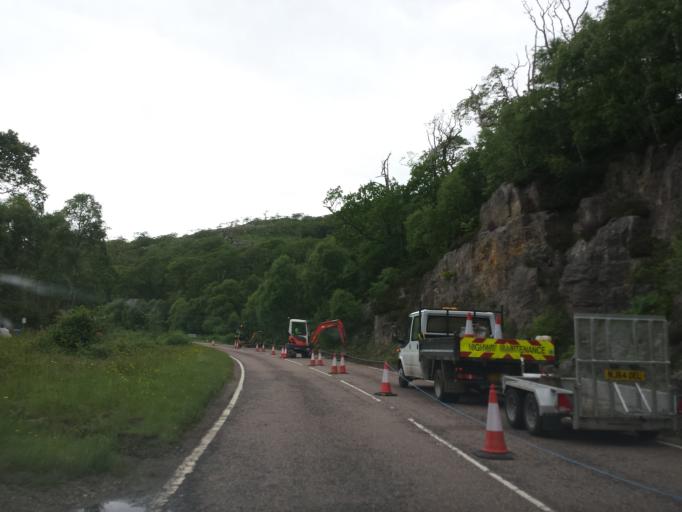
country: GB
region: Scotland
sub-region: Argyll and Bute
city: Isle Of Mull
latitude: 56.8962
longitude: -5.7365
